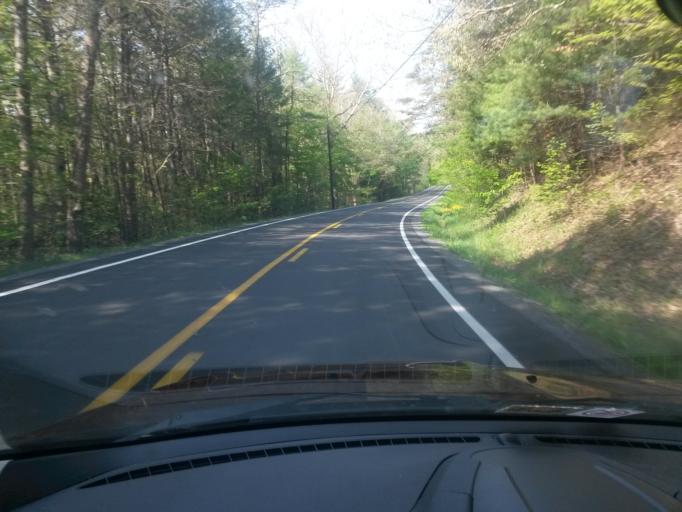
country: US
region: West Virginia
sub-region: Pocahontas County
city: Marlinton
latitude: 38.0229
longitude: -80.0429
